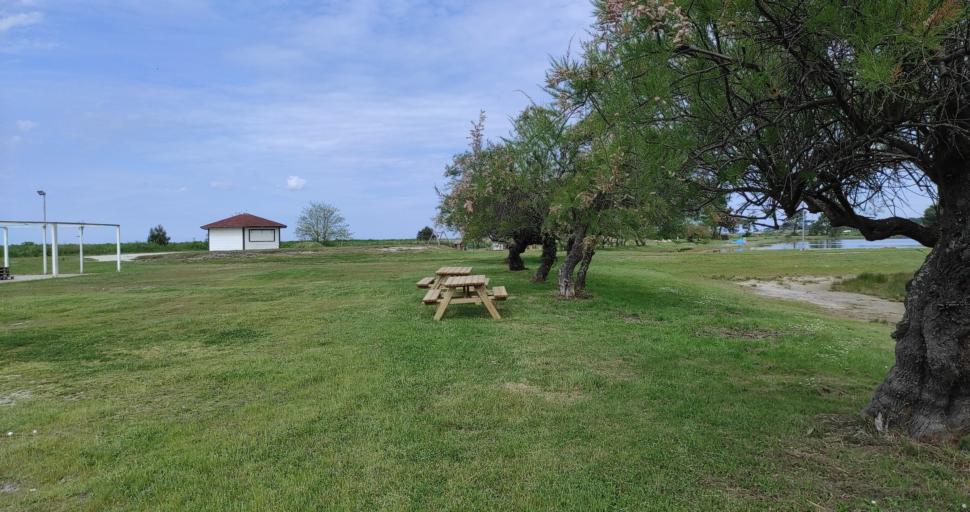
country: FR
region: Aquitaine
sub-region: Departement de la Gironde
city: Lanton
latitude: 44.7021
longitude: -1.0495
